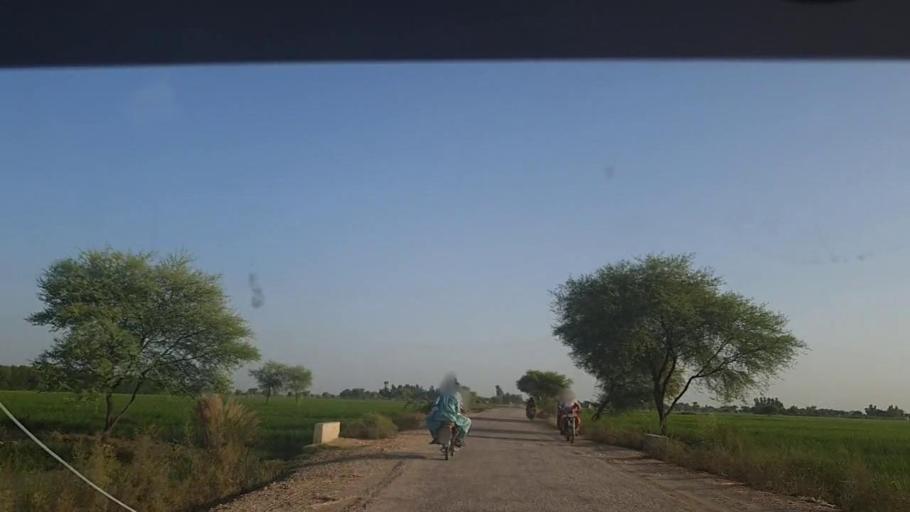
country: PK
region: Sindh
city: Thul
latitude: 28.2106
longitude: 68.8702
